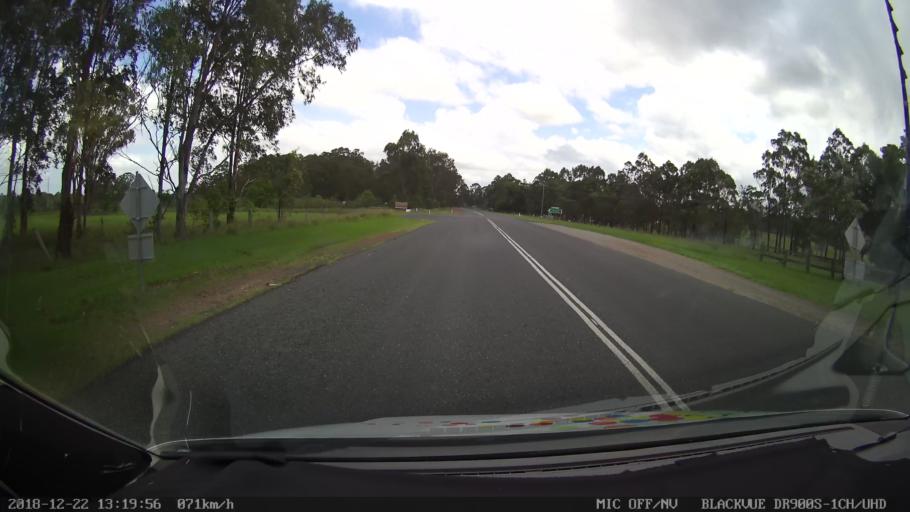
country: AU
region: New South Wales
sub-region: Clarence Valley
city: South Grafton
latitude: -29.7611
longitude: 152.9304
